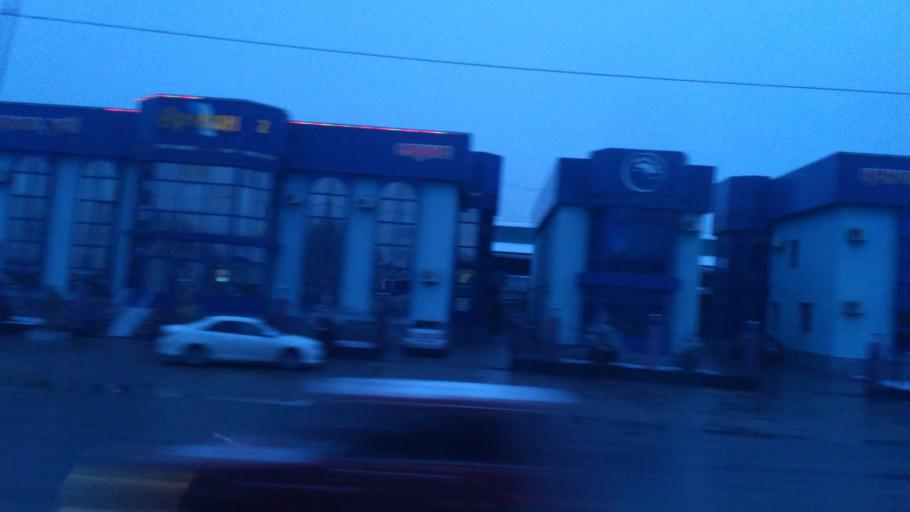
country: KZ
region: Ongtustik Qazaqstan
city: Shymkent
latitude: 42.3548
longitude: 69.5264
